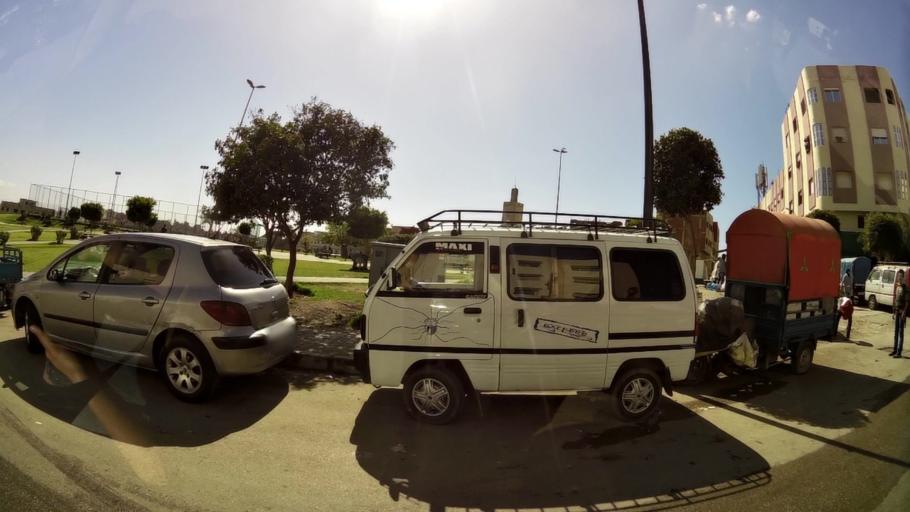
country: MA
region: Tanger-Tetouan
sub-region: Tanger-Assilah
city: Tangier
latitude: 35.7421
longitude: -5.8128
